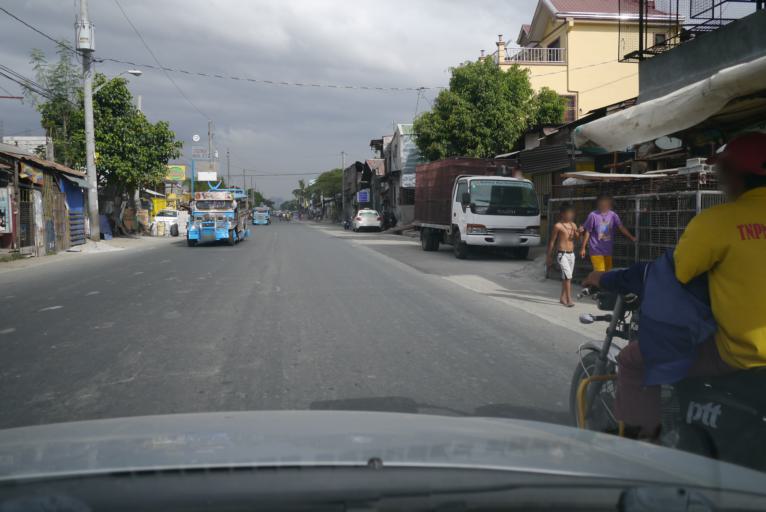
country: PH
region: Calabarzon
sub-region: Province of Rizal
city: Taytay
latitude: 14.5578
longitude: 121.1147
